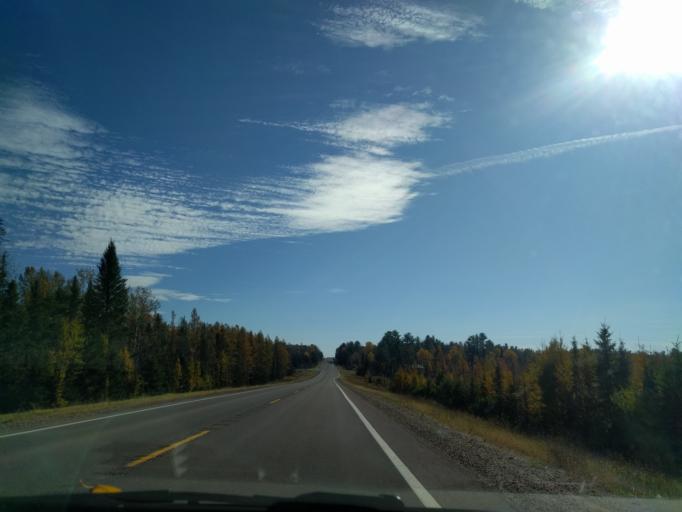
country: US
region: Michigan
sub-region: Marquette County
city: West Ishpeming
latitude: 46.3663
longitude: -87.9879
